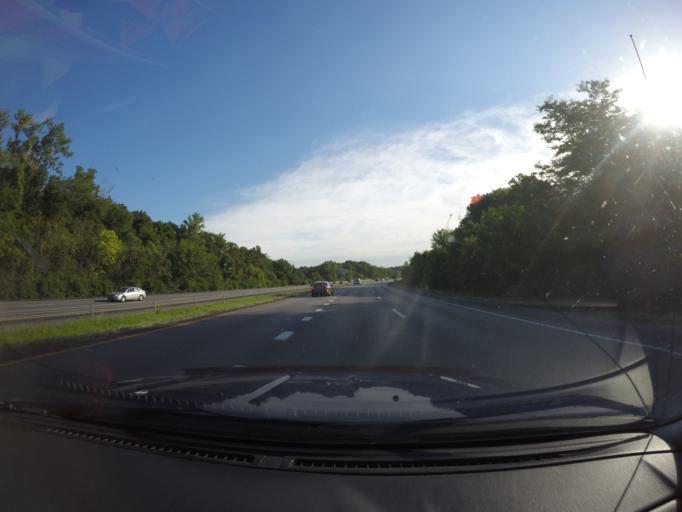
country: US
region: Missouri
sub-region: Platte County
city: Riverside
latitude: 39.1850
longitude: -94.6213
